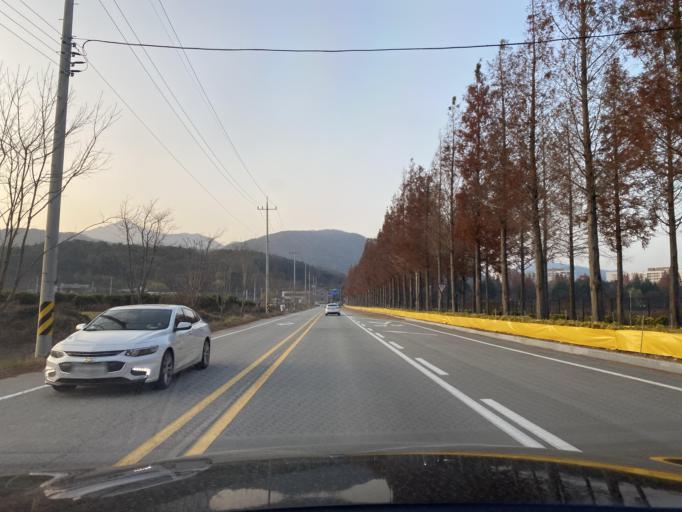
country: KR
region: Chungcheongnam-do
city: Hongsung
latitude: 36.6877
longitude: 126.6589
